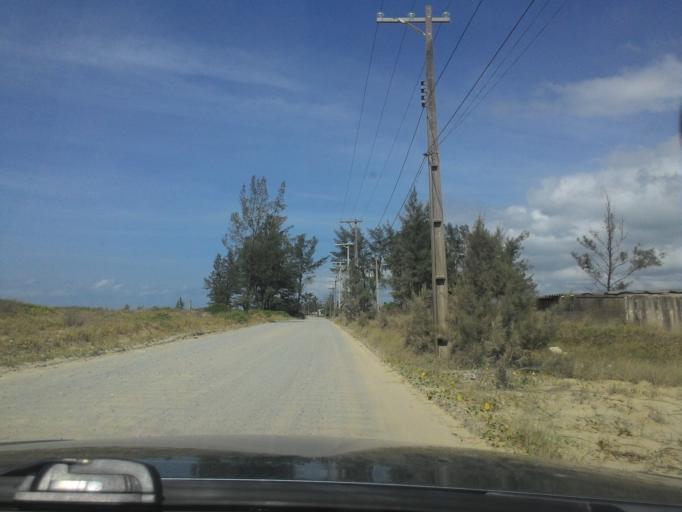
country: BR
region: Sao Paulo
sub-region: Iguape
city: Iguape
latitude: -24.8353
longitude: -47.6747
